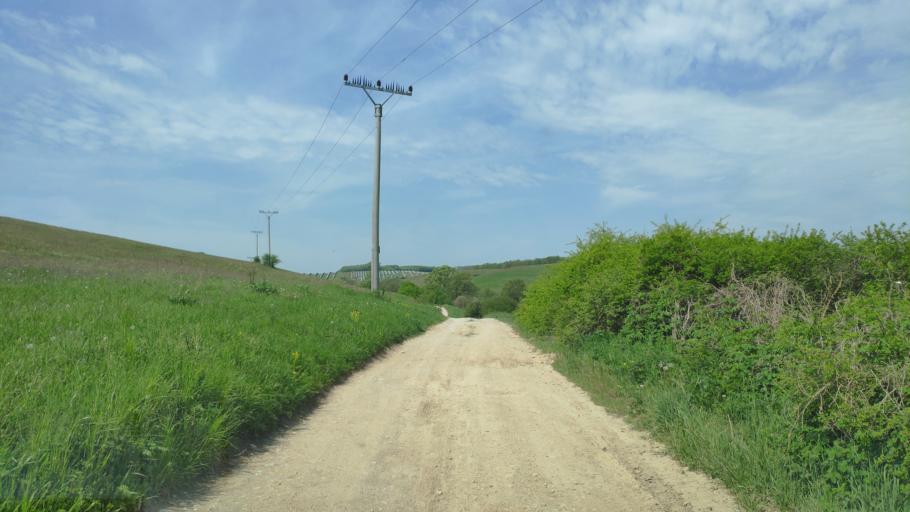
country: SK
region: Banskobystricky
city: Rimavska Sobota
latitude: 48.4310
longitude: 20.2053
